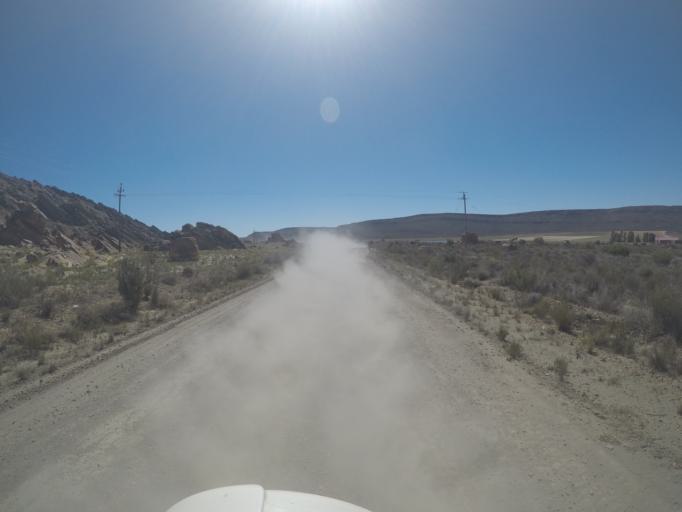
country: ZA
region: Western Cape
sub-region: Cape Winelands District Municipality
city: Ceres
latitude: -32.8449
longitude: 19.4474
